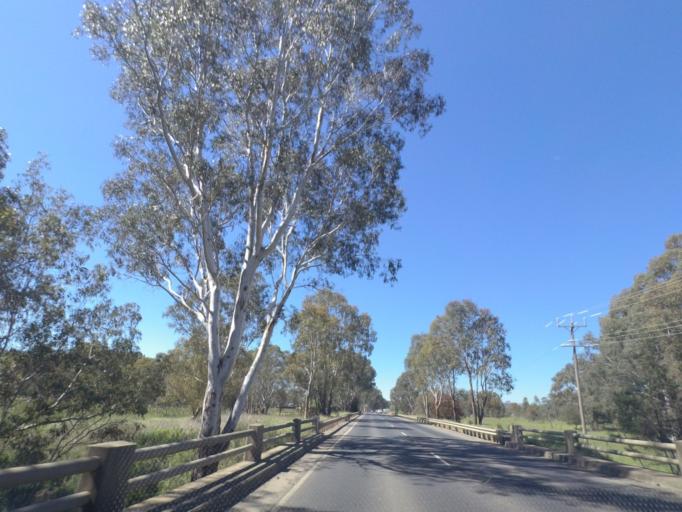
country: AU
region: Victoria
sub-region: Murrindindi
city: Kinglake West
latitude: -37.0253
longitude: 145.1115
